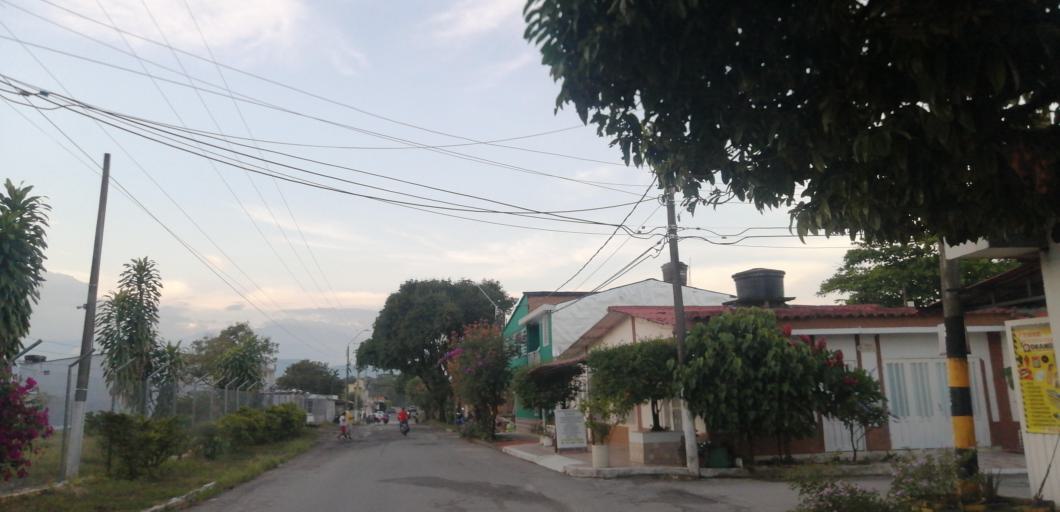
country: CO
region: Meta
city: Acacias
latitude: 3.9957
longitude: -73.7564
